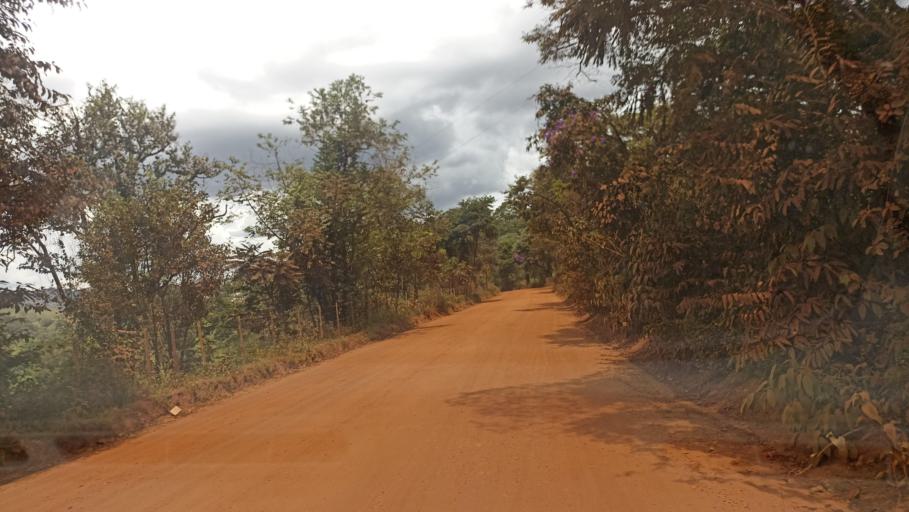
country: BR
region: Minas Gerais
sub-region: Itabirito
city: Itabirito
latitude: -20.3437
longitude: -43.7715
